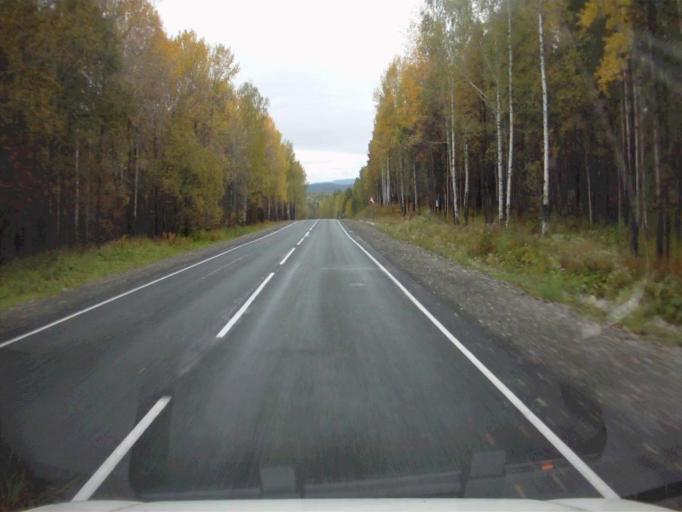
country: RU
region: Chelyabinsk
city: Nyazepetrovsk
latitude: 56.0526
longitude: 59.7417
